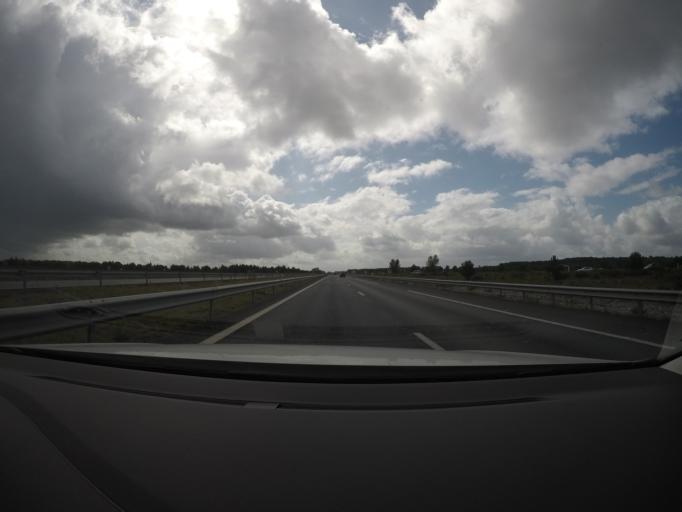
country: FR
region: Aquitaine
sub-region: Departement des Landes
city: Saint-Geours-de-Maremne
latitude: 43.7114
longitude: -1.2283
